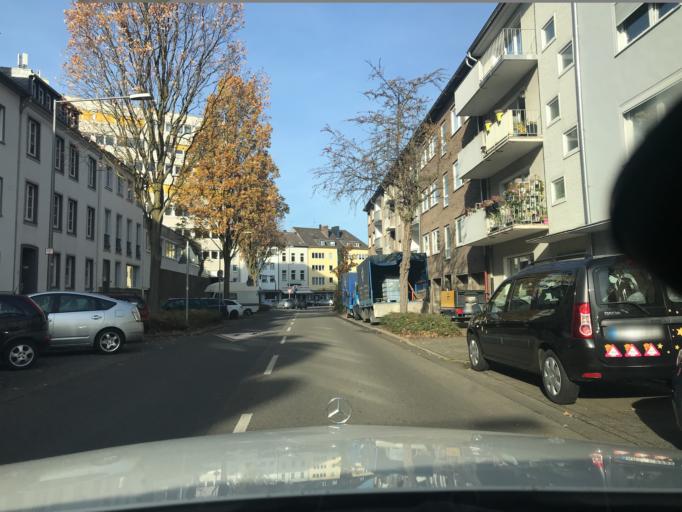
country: DE
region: North Rhine-Westphalia
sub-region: Regierungsbezirk Dusseldorf
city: Krefeld
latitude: 51.3381
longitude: 6.5753
